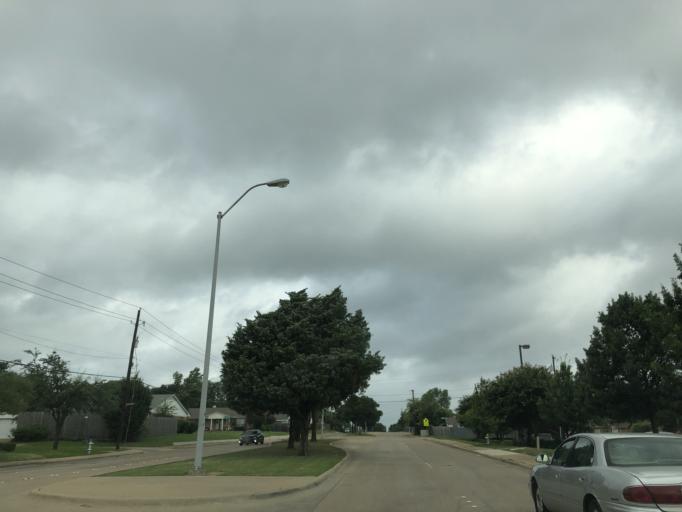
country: US
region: Texas
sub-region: Dallas County
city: Mesquite
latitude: 32.8347
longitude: -96.6348
